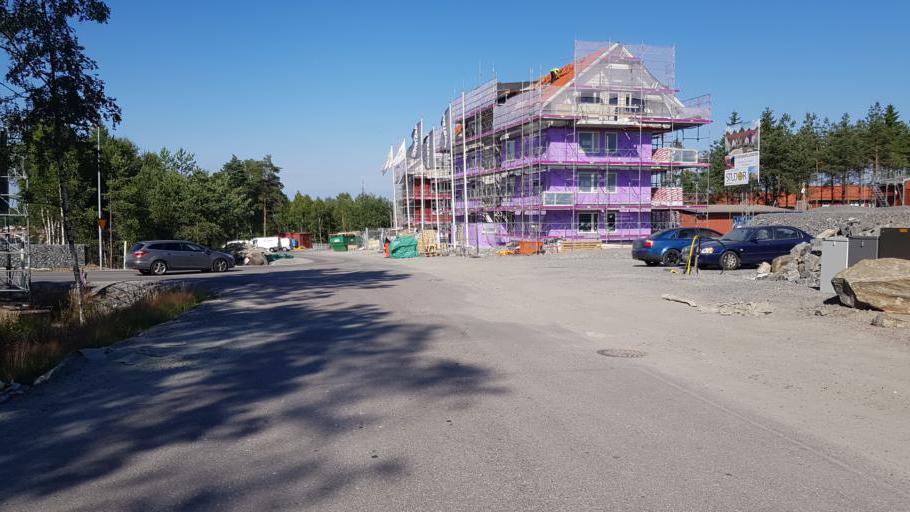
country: SE
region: Vaestra Goetaland
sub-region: Partille Kommun
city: Furulund
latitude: 57.7000
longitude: 12.1440
